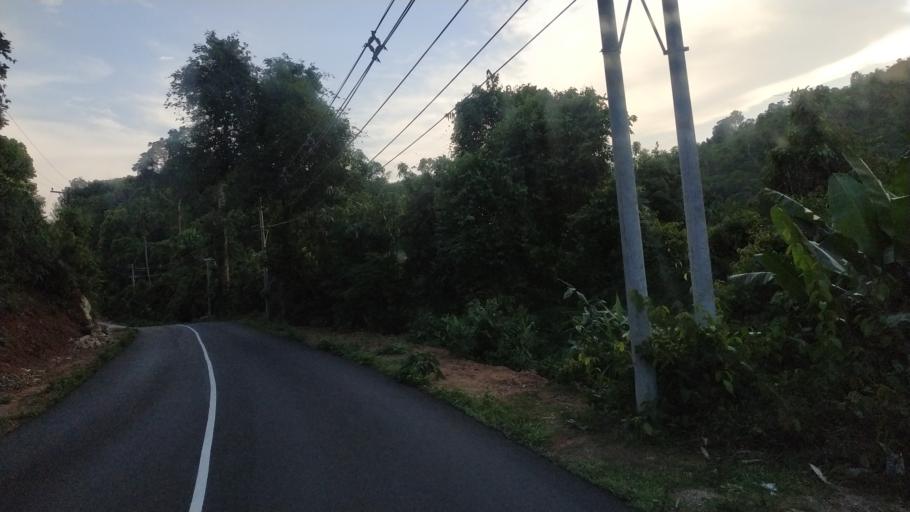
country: MM
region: Mon
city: Kyaikto
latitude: 17.4311
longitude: 97.0909
